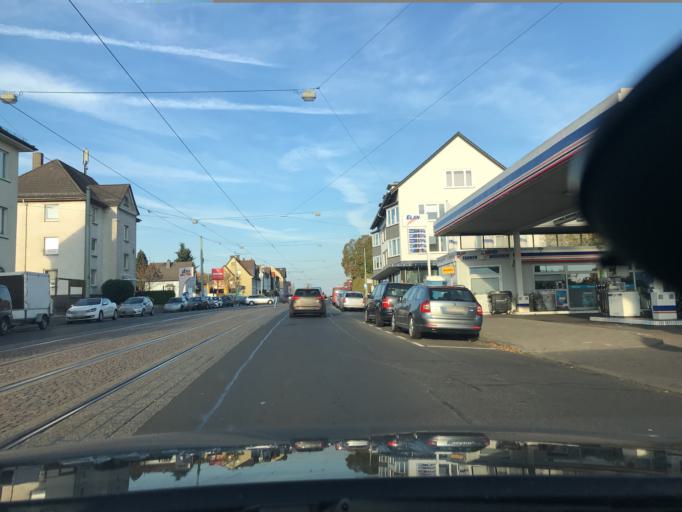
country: DE
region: Hesse
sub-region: Regierungsbezirk Kassel
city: Fuldabruck
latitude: 51.2886
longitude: 9.4712
